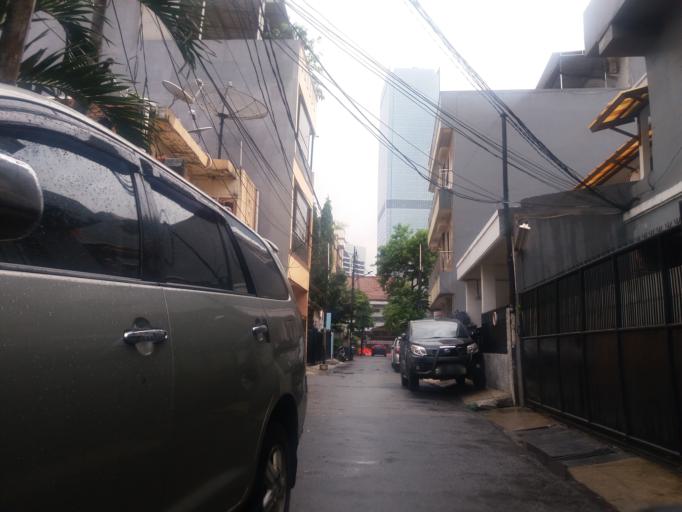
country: ID
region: Jakarta Raya
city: Jakarta
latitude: -6.2148
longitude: 106.8247
